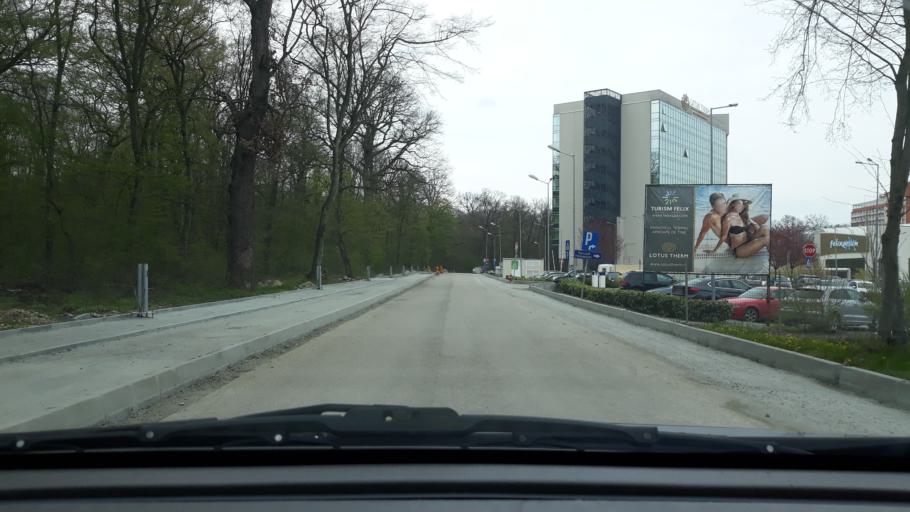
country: RO
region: Bihor
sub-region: Comuna Sanmartin
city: Sanmartin
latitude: 46.9882
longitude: 21.9760
